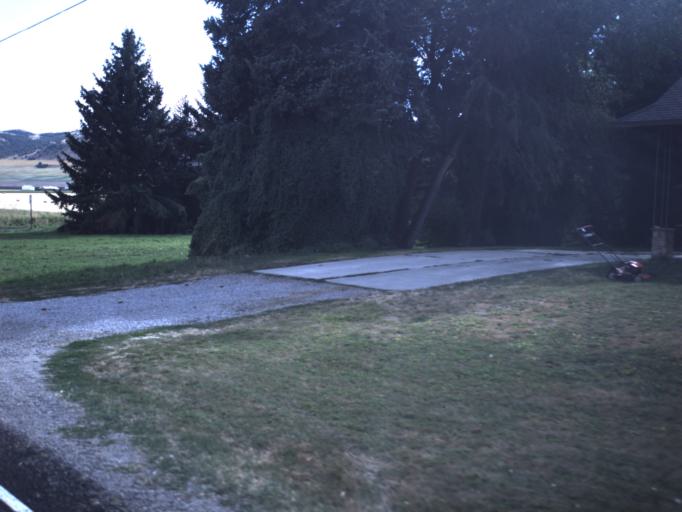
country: US
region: Utah
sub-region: Cache County
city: Benson
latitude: 41.9144
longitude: -112.0453
